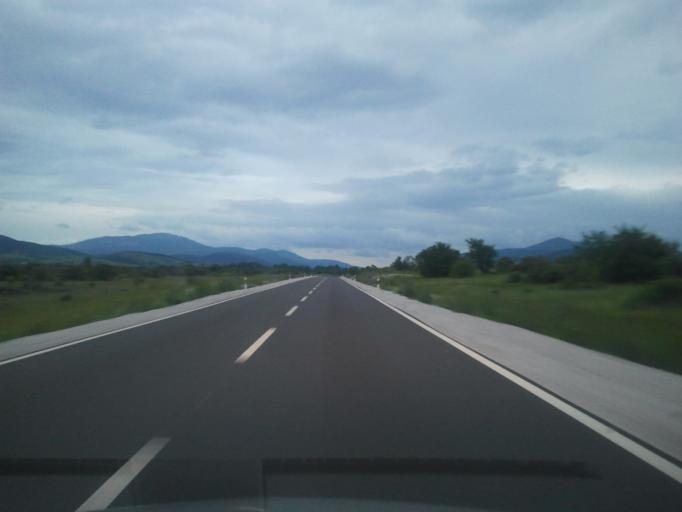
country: HR
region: Zadarska
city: Gracac
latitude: 44.3316
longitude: 15.8627
